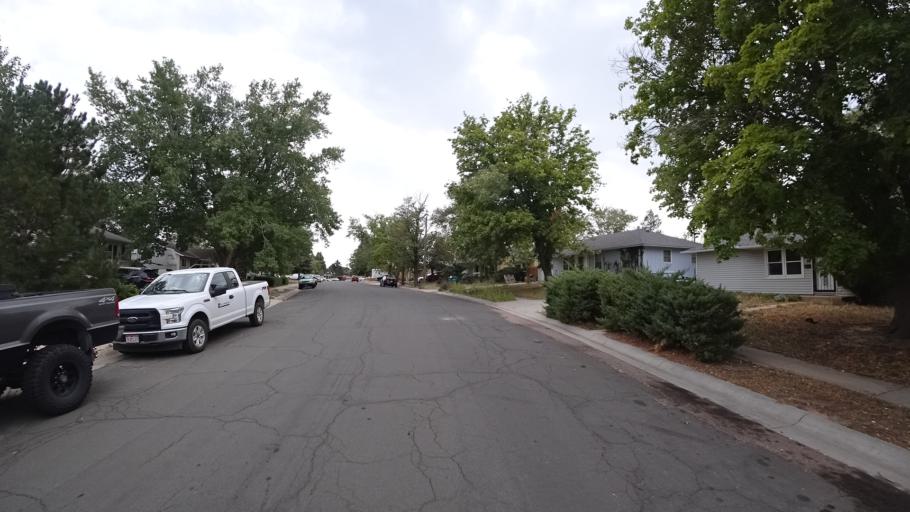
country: US
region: Colorado
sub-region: El Paso County
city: Colorado Springs
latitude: 38.8345
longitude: -104.7835
